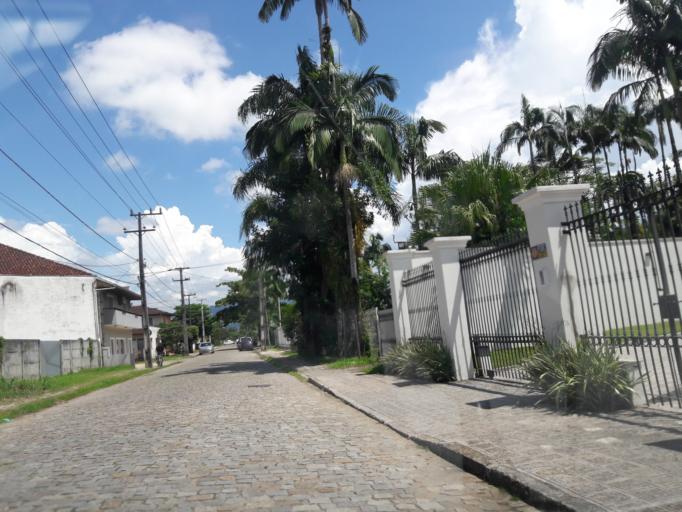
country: BR
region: Parana
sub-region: Antonina
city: Antonina
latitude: -25.4724
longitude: -48.8309
